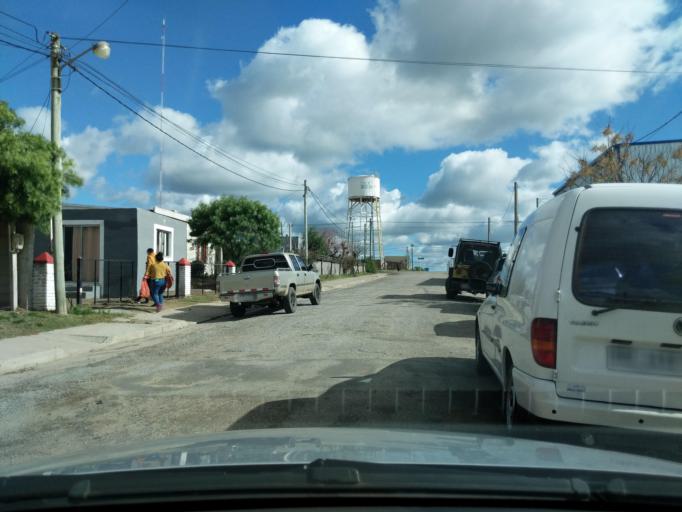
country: UY
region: Florida
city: Florida
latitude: -34.0870
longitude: -56.2366
